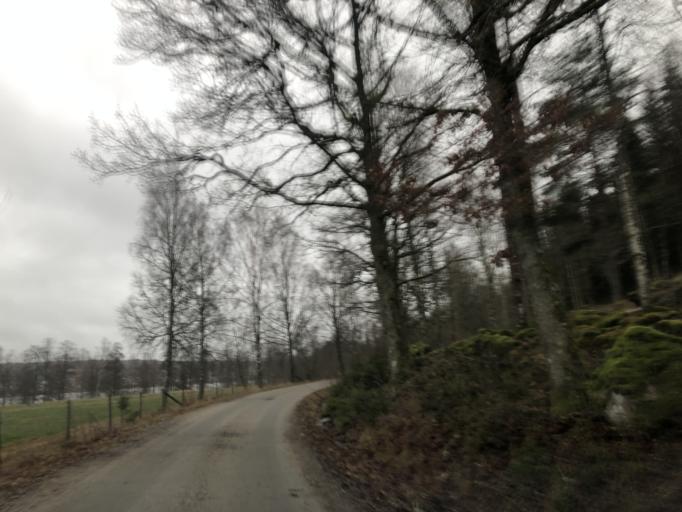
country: SE
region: Vaestra Goetaland
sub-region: Ulricehamns Kommun
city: Ulricehamn
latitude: 57.7936
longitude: 13.3903
